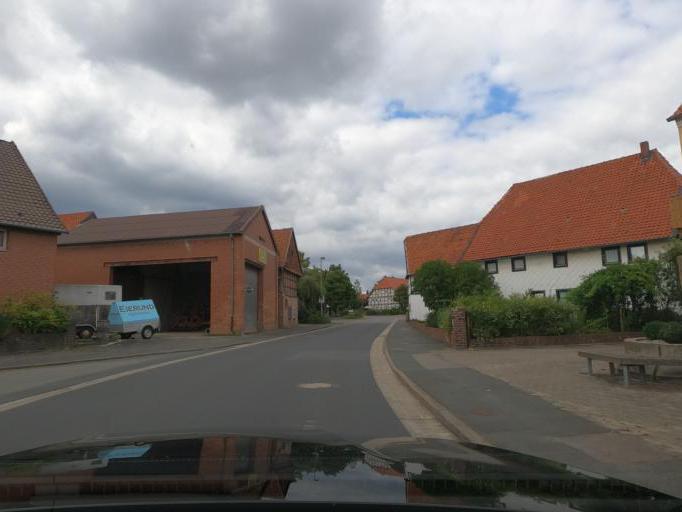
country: DE
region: Lower Saxony
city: Algermissen
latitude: 52.2735
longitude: 9.9518
